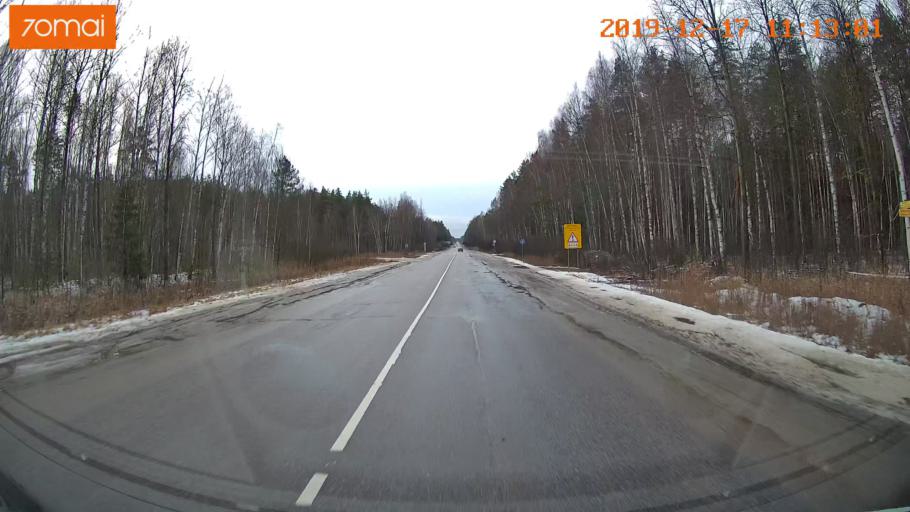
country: RU
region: Vladimir
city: Gus'-Khrustal'nyy
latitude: 55.5686
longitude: 40.6229
